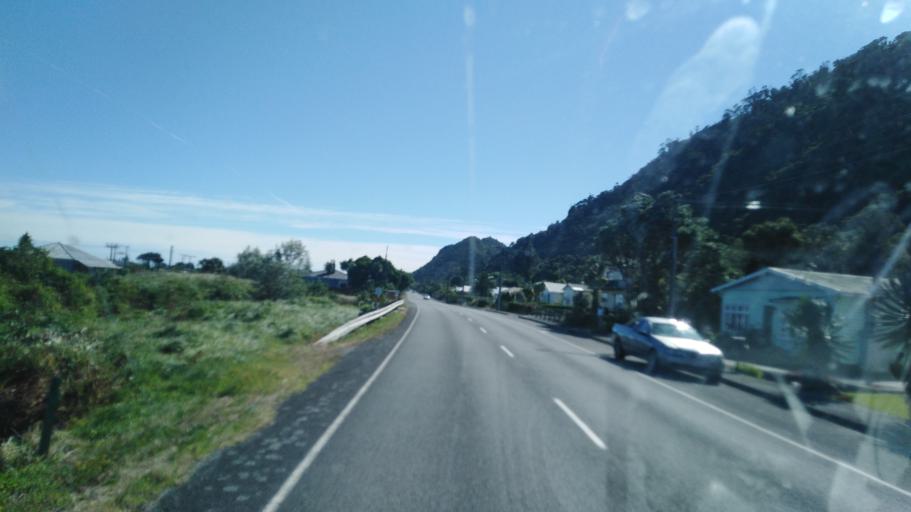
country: NZ
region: West Coast
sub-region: Buller District
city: Westport
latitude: -41.6377
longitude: 171.8472
